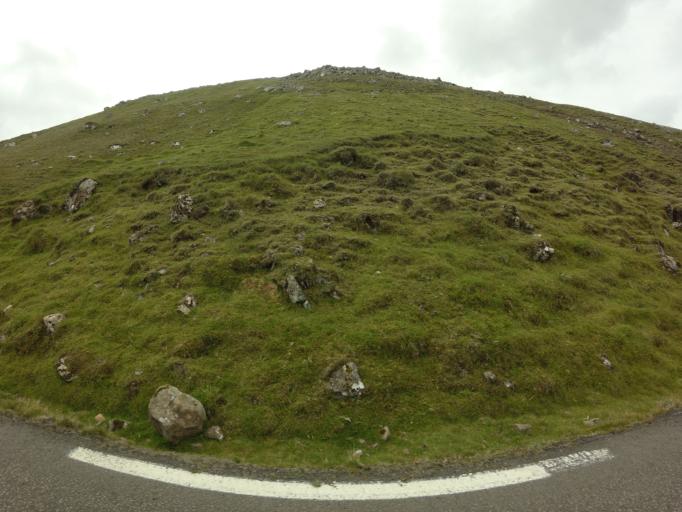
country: FO
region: Suduroy
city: Tvoroyri
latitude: 61.5253
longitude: -6.8298
